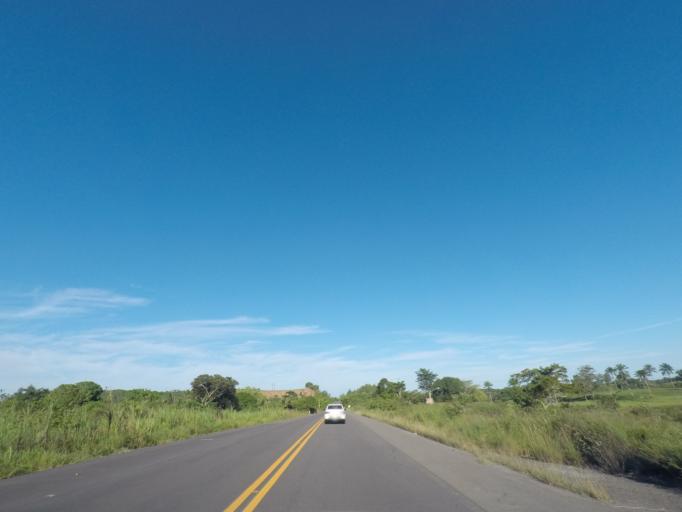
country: BR
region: Bahia
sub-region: Nazare
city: Nazare
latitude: -13.0170
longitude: -38.9836
